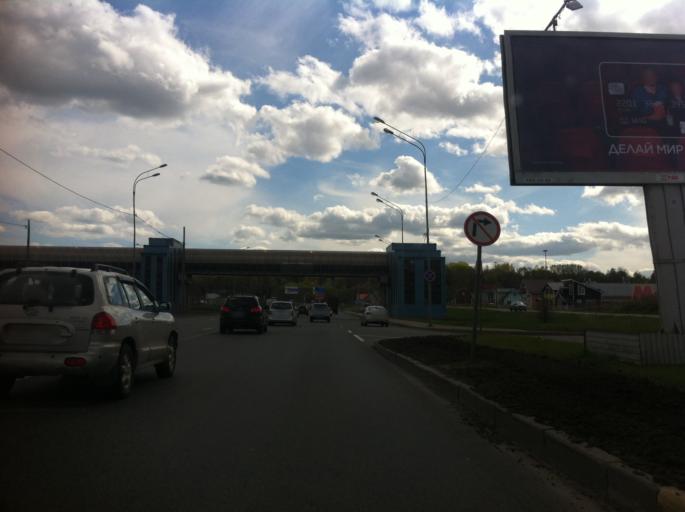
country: RU
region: St.-Petersburg
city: Aleksandrovskaya
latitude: 59.7817
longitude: 30.3250
